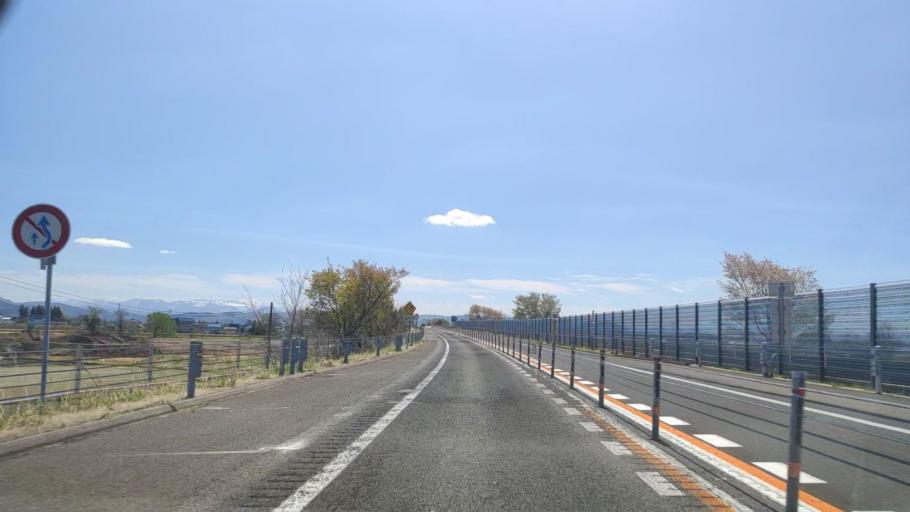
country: JP
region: Akita
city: Yokotemachi
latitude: 39.3358
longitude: 140.5030
